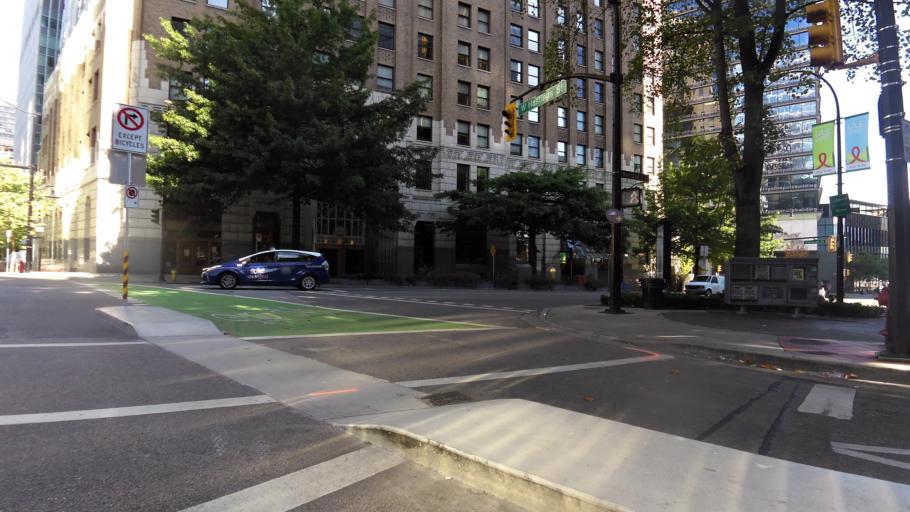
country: CA
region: British Columbia
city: West End
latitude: 49.2872
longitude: -123.1168
